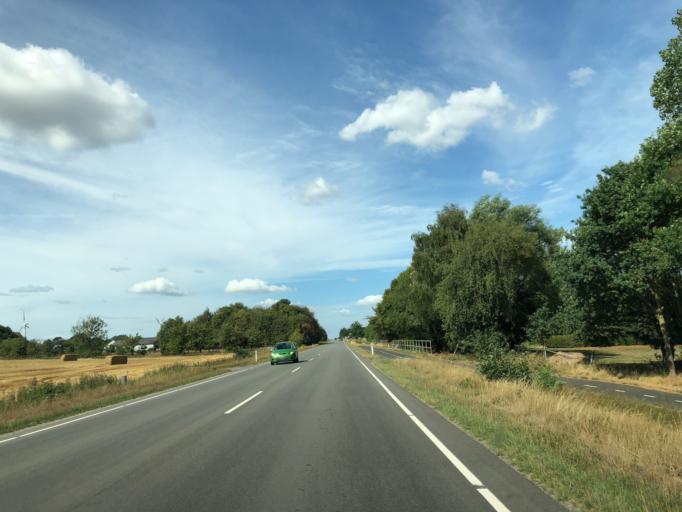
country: DK
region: Central Jutland
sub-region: Ikast-Brande Kommune
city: Bording Kirkeby
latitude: 56.1418
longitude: 9.2555
